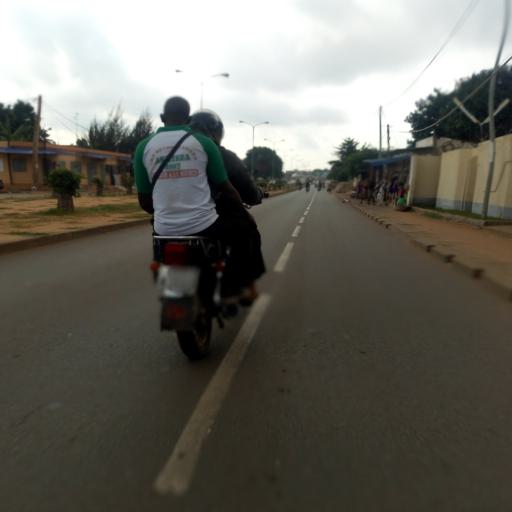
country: TG
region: Maritime
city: Lome
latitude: 6.1891
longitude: 1.2535
